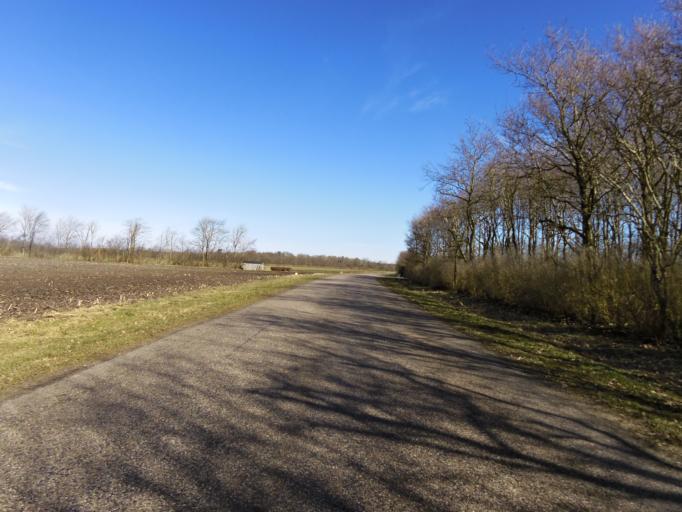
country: DK
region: South Denmark
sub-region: Tonder Kommune
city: Toftlund
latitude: 55.2362
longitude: 9.0774
